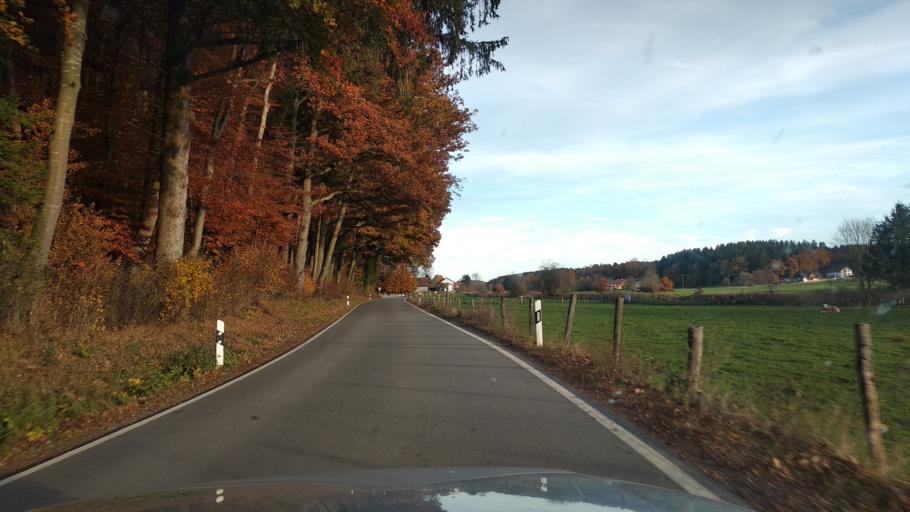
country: DE
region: Bavaria
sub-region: Upper Bavaria
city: Bruck
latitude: 48.0399
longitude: 11.9182
